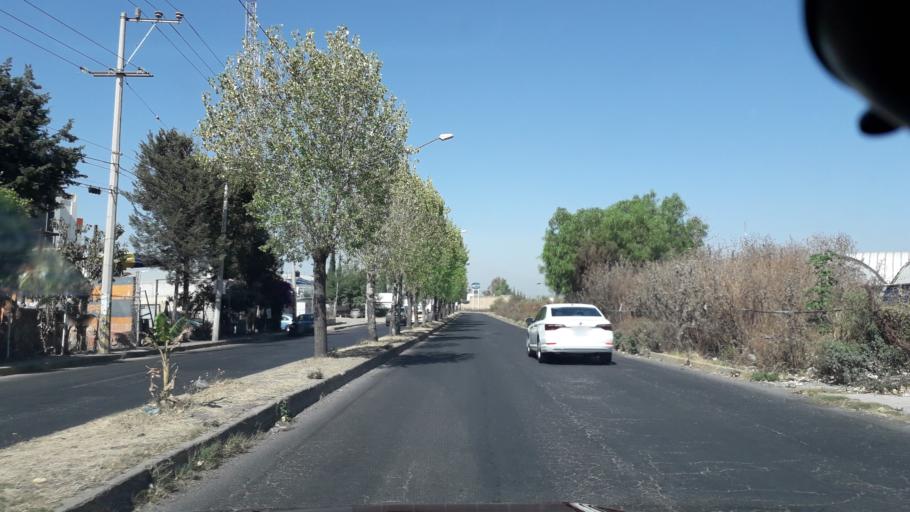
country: MX
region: Puebla
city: Puebla
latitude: 19.0807
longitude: -98.2130
